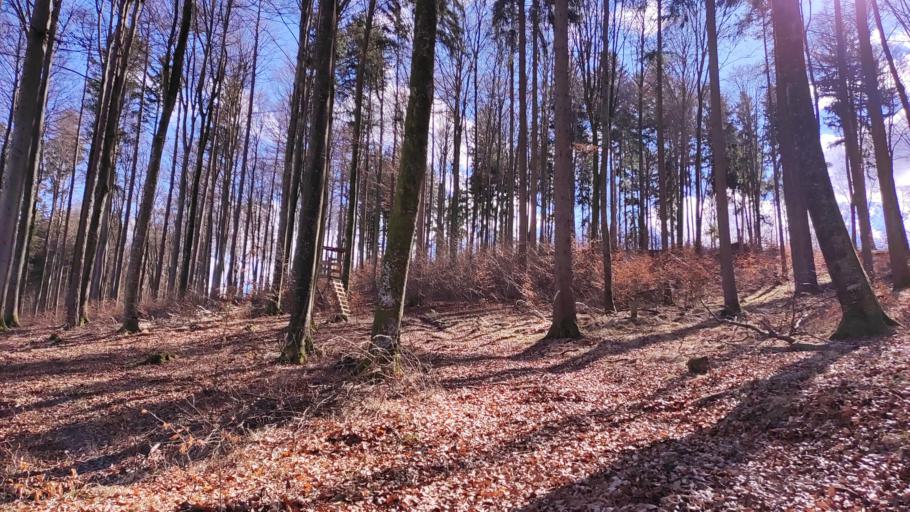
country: DE
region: Bavaria
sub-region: Swabia
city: Zusmarshausen
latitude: 48.4279
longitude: 10.6106
